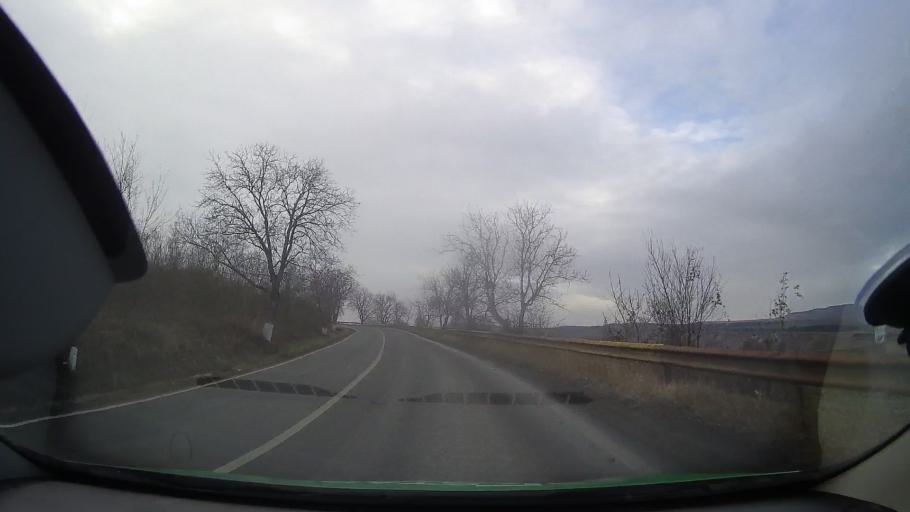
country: RO
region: Mures
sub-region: Municipiul Tarnaveni
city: Bobohalma
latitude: 46.3594
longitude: 24.2695
